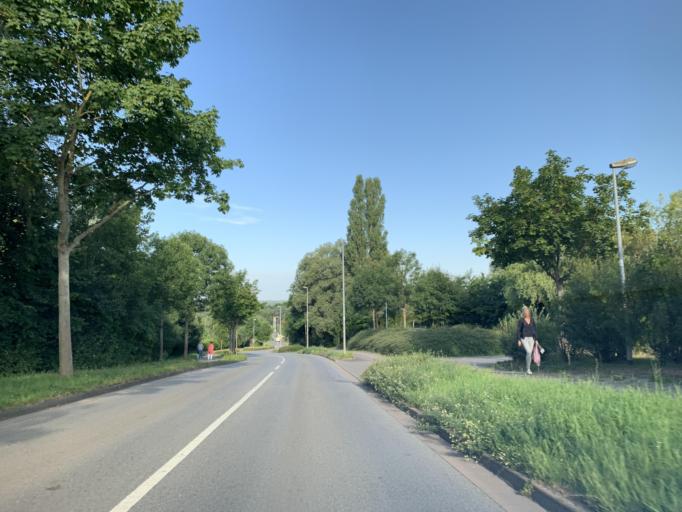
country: DE
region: Mecklenburg-Vorpommern
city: Neubrandenburg
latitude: 53.5856
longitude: 13.2778
